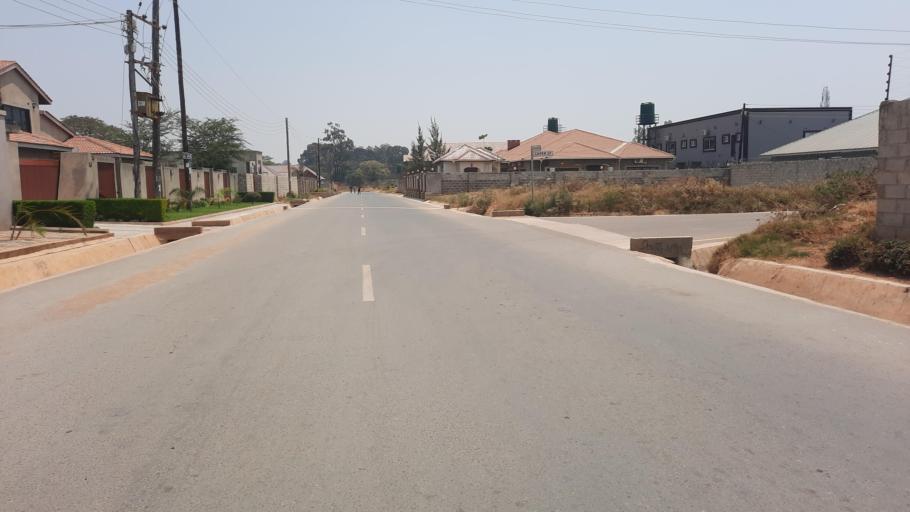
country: ZM
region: Lusaka
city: Lusaka
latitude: -15.3916
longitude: 28.3852
